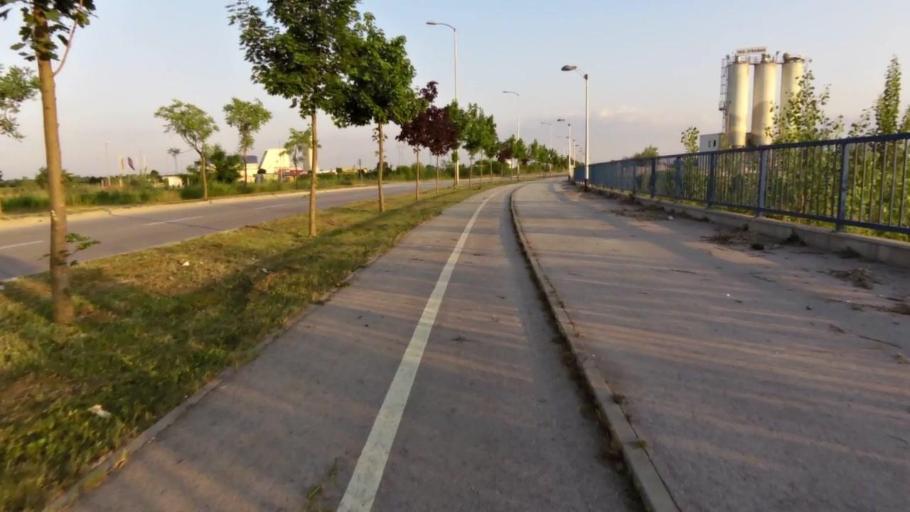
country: HR
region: Grad Zagreb
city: Dubrava
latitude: 45.7981
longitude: 16.0788
